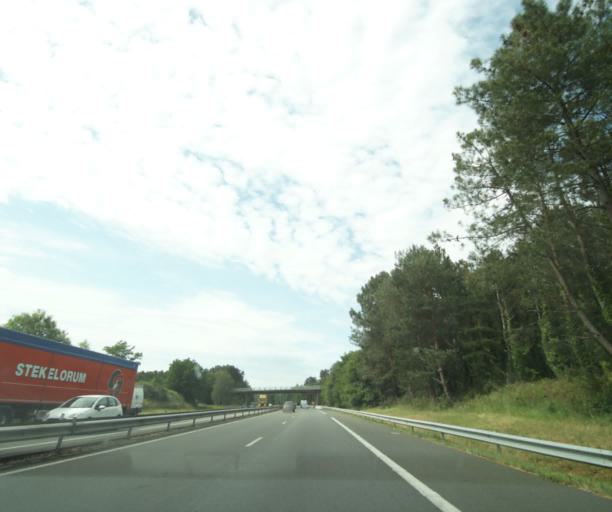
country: FR
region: Pays de la Loire
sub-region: Departement de Maine-et-Loire
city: Seiches-sur-le-Loir
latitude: 47.5632
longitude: -0.3305
